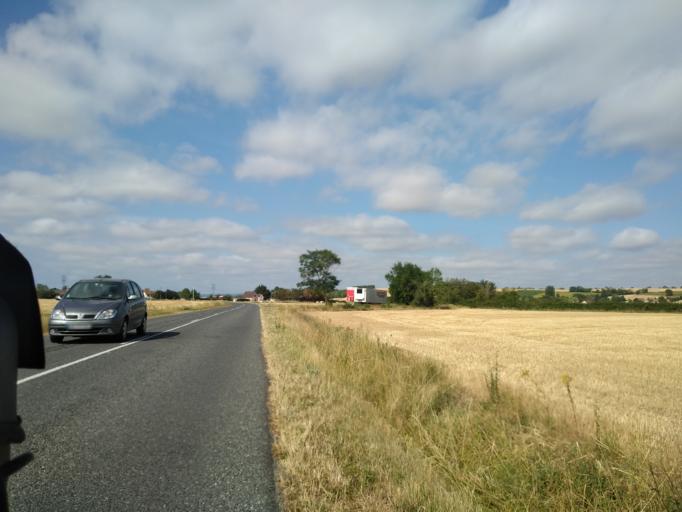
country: FR
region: Auvergne
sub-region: Departement de l'Allier
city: Saint-Pourcain-sur-Sioule
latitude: 46.2835
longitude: 3.2386
